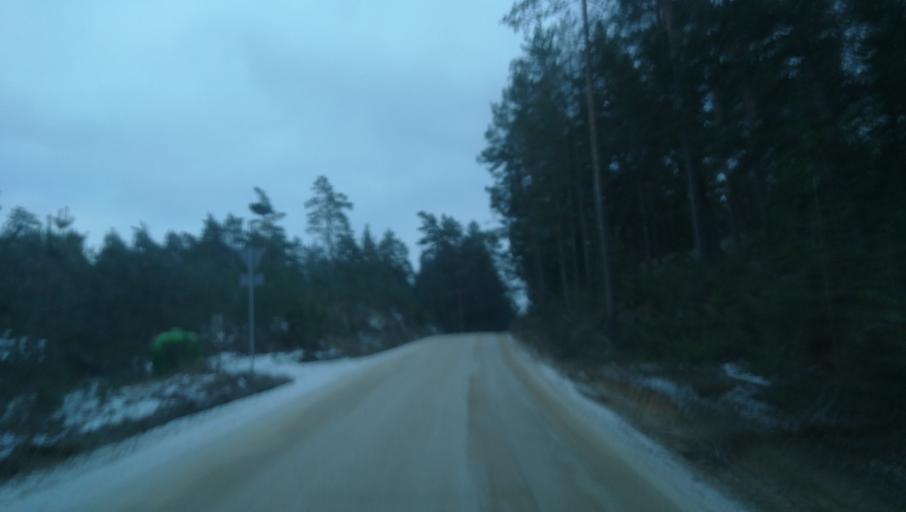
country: LV
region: Garkalne
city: Garkalne
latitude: 57.0320
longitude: 24.3816
